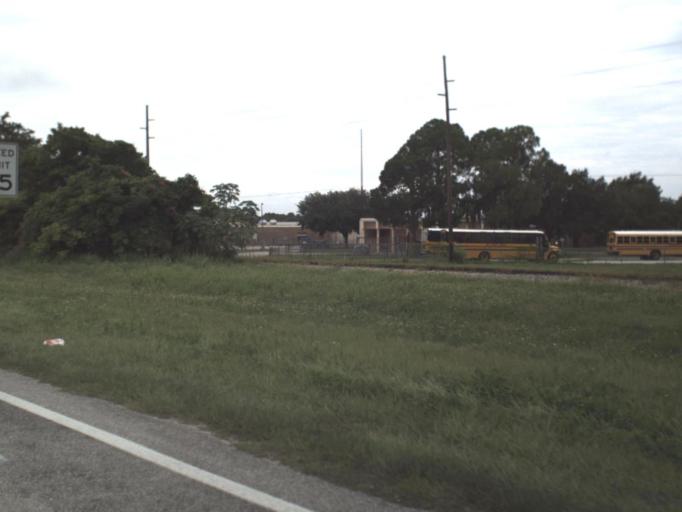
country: US
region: Florida
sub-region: Polk County
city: Eagle Lake
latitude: 27.9741
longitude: -81.7630
